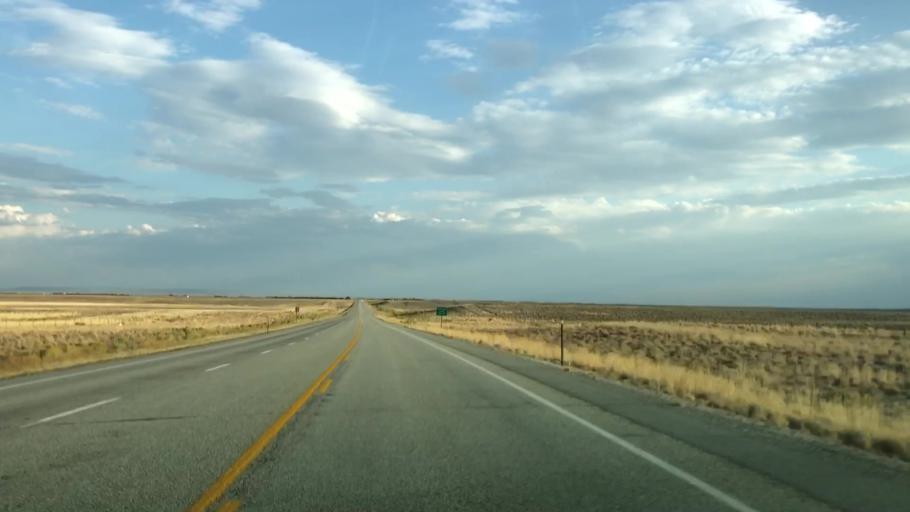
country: US
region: Wyoming
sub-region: Sweetwater County
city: North Rock Springs
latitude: 42.1886
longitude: -109.4801
